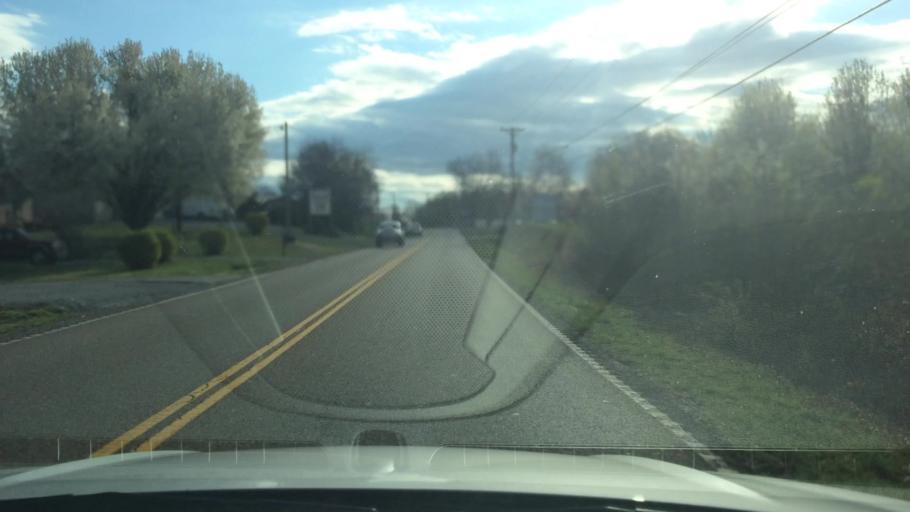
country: US
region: Tennessee
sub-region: Sevier County
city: Seymour
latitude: 35.8747
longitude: -83.7503
